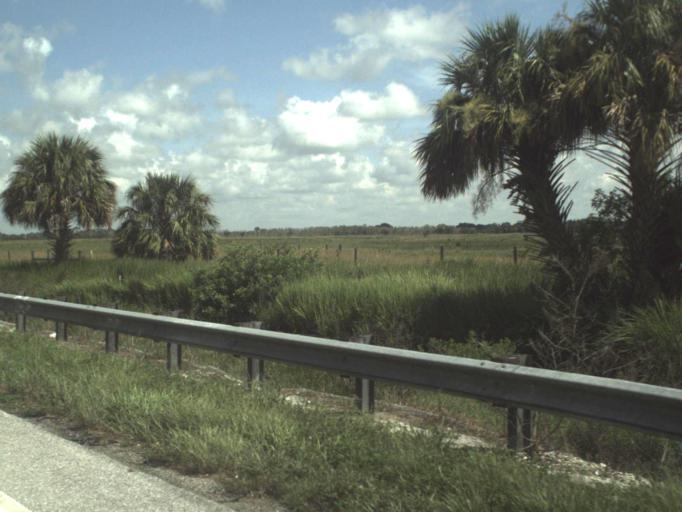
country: US
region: Florida
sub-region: Martin County
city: Indiantown
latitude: 27.0757
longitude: -80.5515
